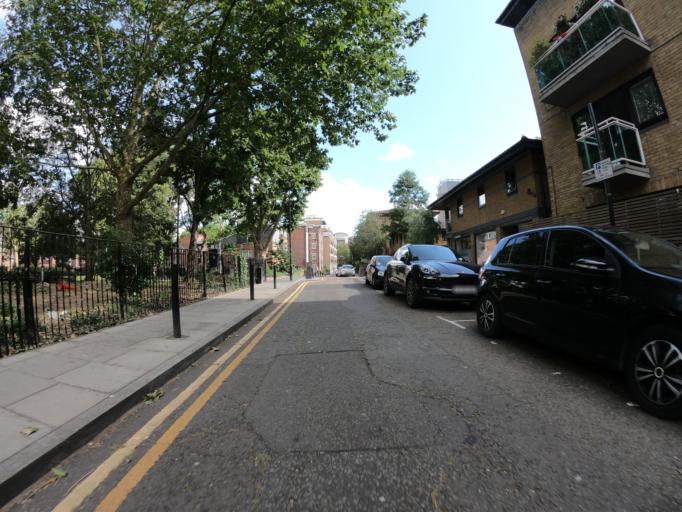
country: GB
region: England
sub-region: Greater London
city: Bethnal Green
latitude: 51.5097
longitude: -0.0709
